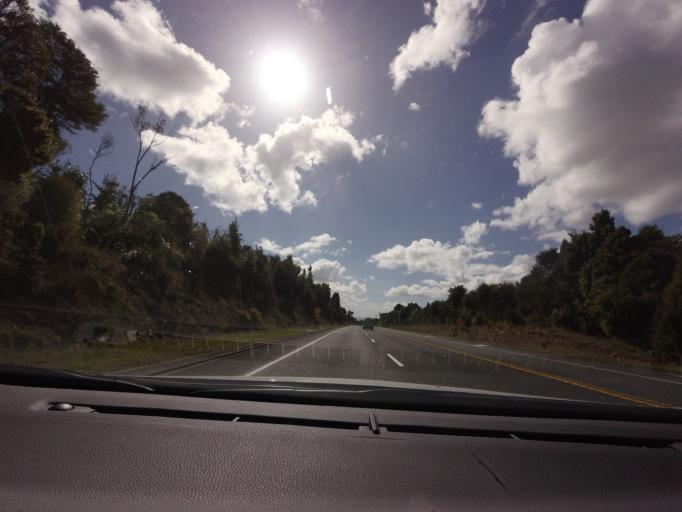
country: NZ
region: Waikato
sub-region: South Waikato District
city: Tokoroa
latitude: -38.0168
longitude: 175.9505
